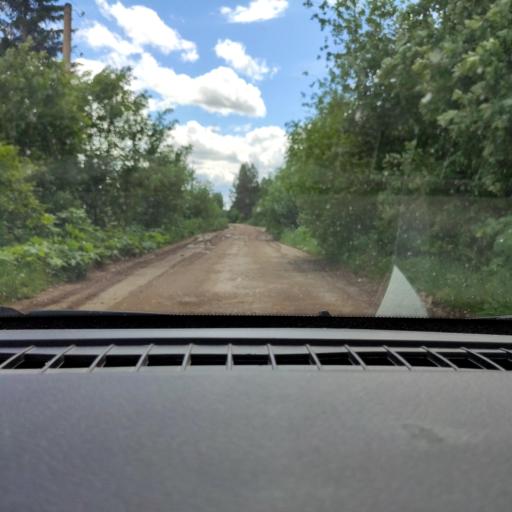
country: RU
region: Perm
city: Overyata
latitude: 58.1378
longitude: 55.8222
